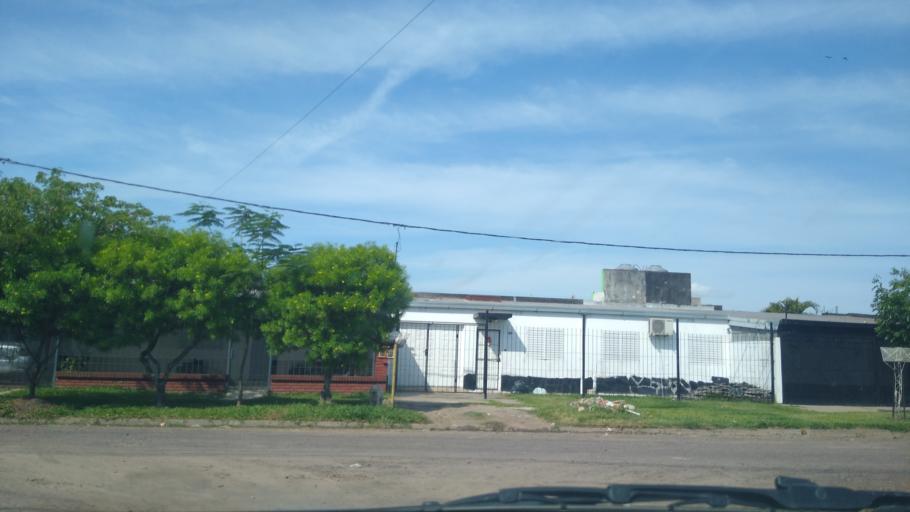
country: AR
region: Chaco
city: Puerto Vilelas
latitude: -27.4974
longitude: -58.9609
